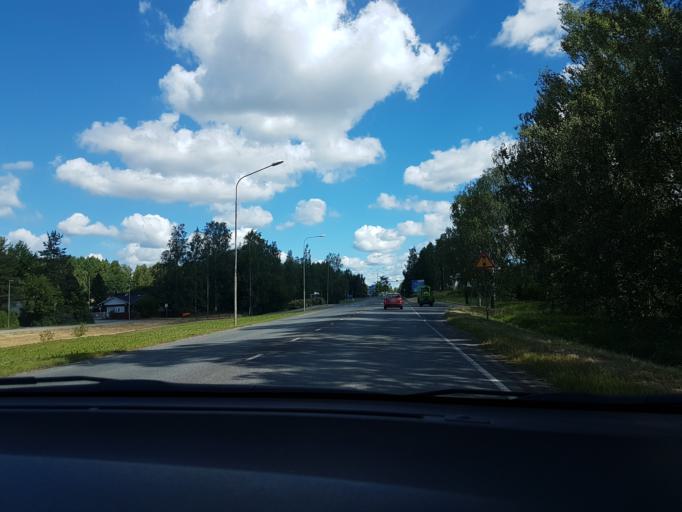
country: FI
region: Uusimaa
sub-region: Helsinki
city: Kerava
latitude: 60.3920
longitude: 25.1011
